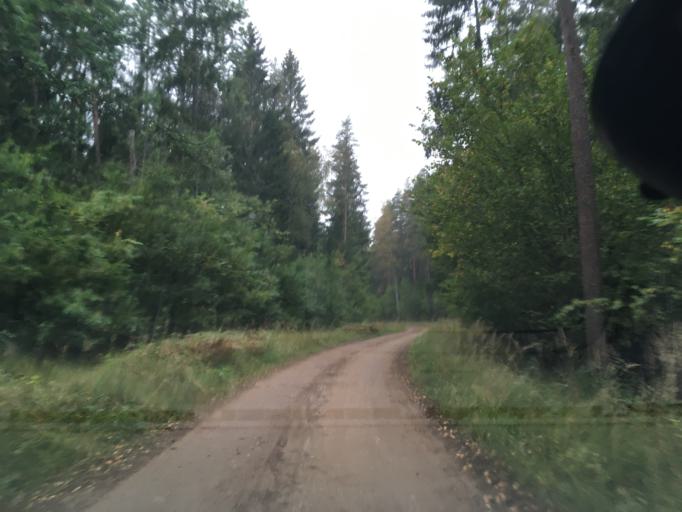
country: LV
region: Kuldigas Rajons
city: Kuldiga
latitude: 56.9872
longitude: 22.0039
